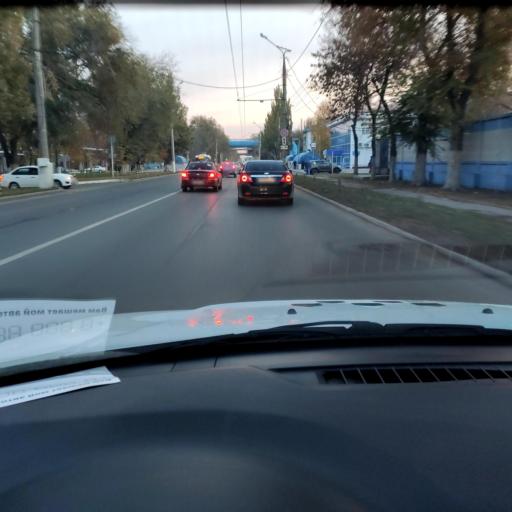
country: RU
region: Samara
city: Tol'yatti
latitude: 53.5544
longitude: 49.4507
